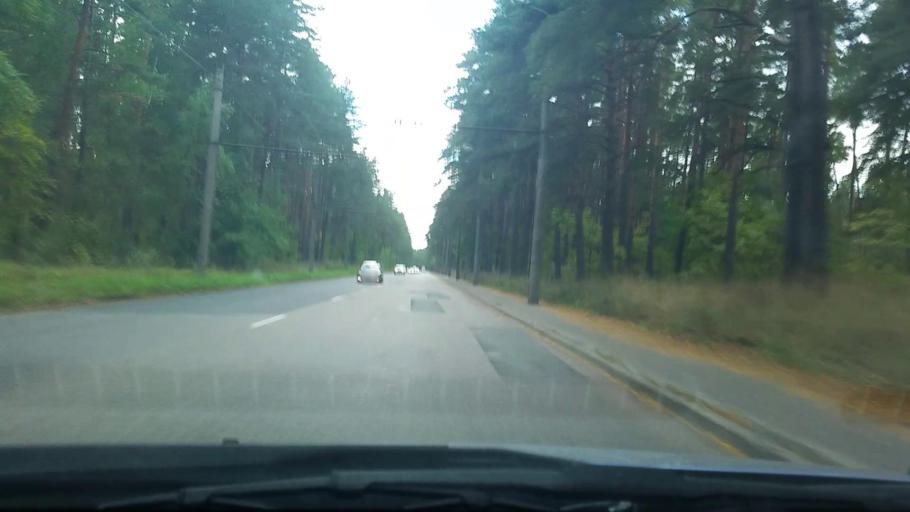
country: LV
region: Stopini
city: Ulbroka
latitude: 56.9629
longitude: 24.2179
